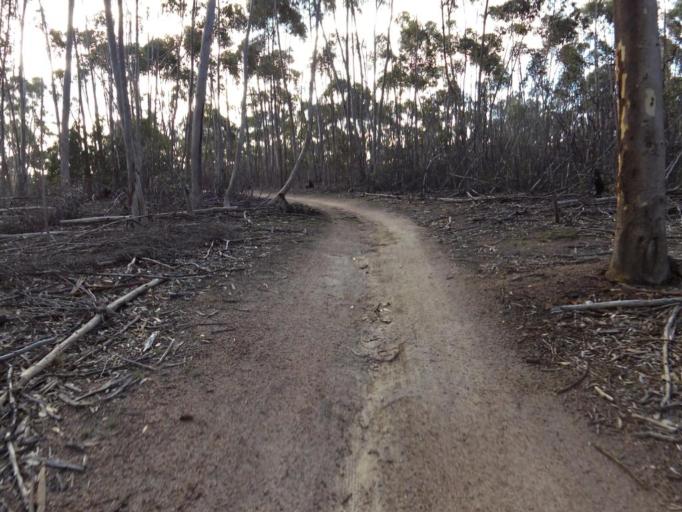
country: AU
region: Victoria
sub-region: Greater Geelong
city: Lara
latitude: -37.9436
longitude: 144.4099
